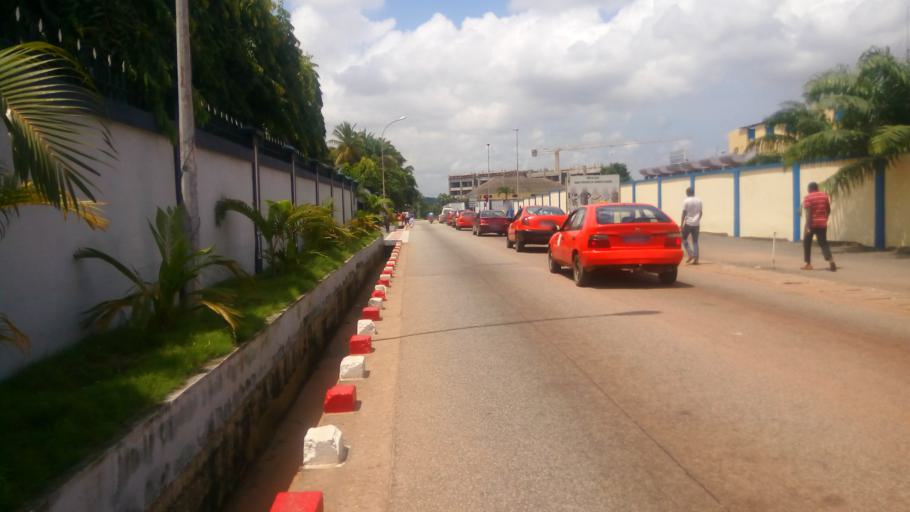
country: CI
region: Lagunes
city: Abidjan
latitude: 5.3360
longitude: -4.0227
